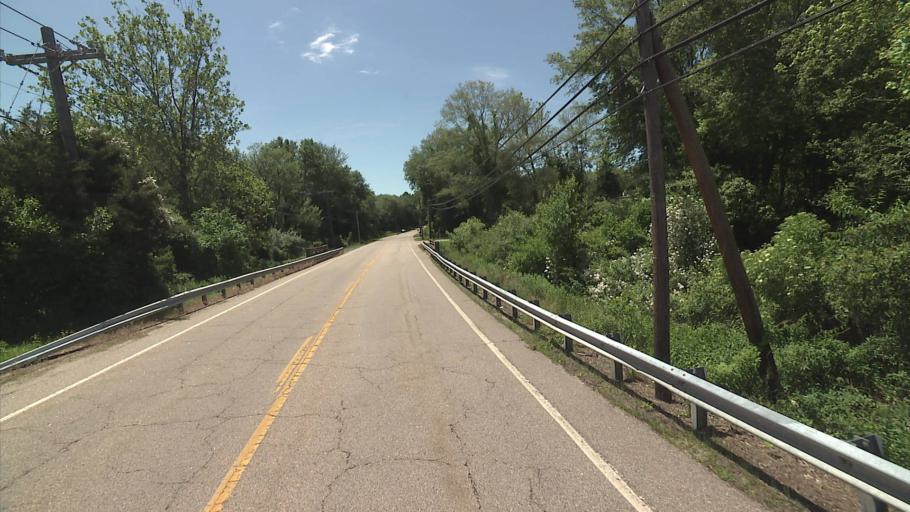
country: US
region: Connecticut
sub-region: New London County
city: Pawcatuck
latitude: 41.4106
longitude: -71.8449
